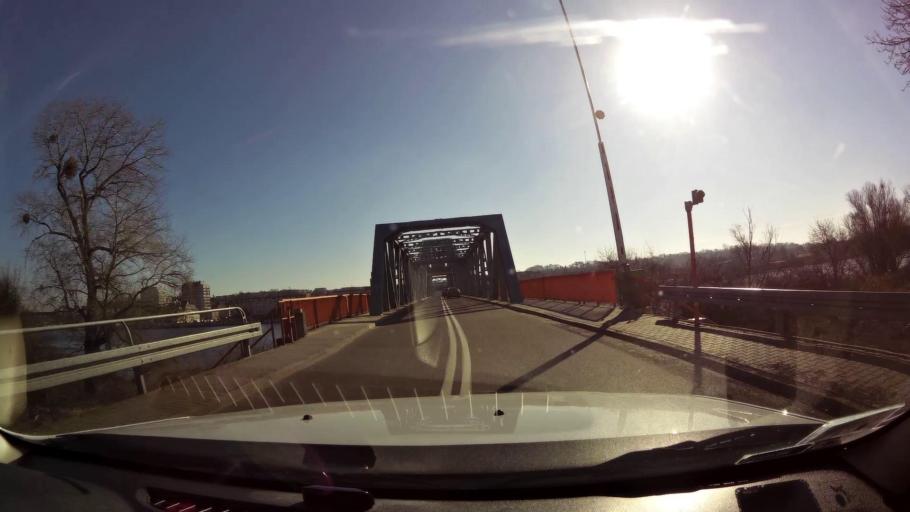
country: PL
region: West Pomeranian Voivodeship
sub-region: Powiat gryfinski
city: Gryfino
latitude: 53.2530
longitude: 14.4798
